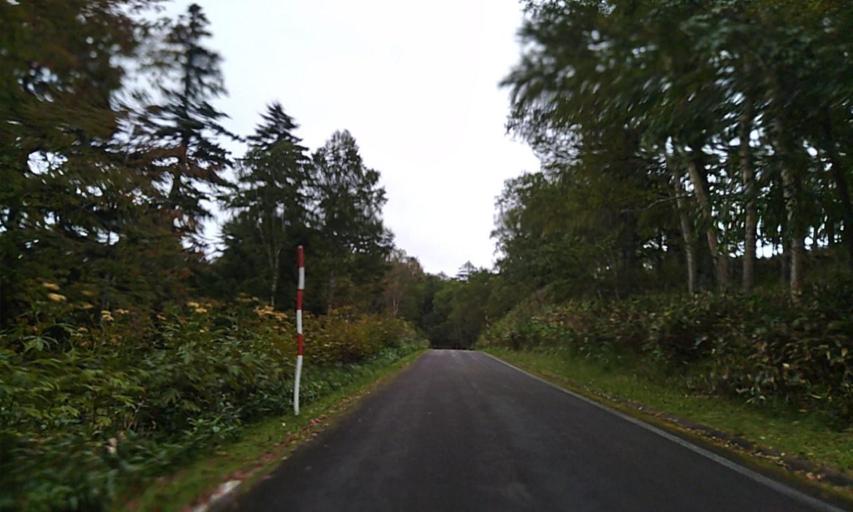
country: JP
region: Hokkaido
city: Bihoro
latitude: 43.5706
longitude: 144.2241
